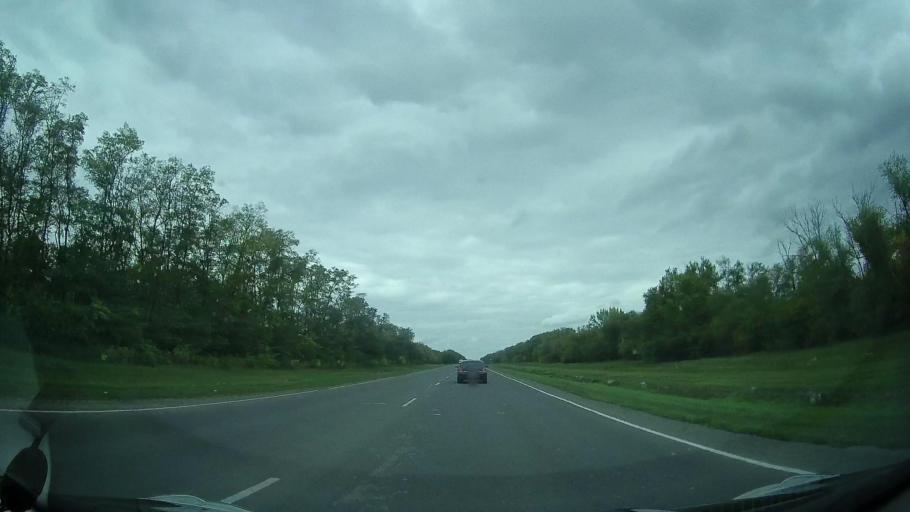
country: RU
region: Rostov
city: Yegorlykskaya
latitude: 46.5984
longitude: 40.6205
